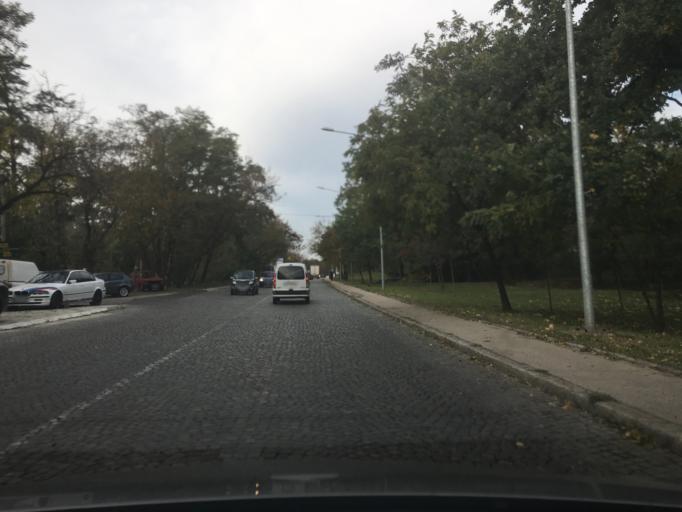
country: RS
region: Central Serbia
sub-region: Belgrade
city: Zemun
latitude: 44.8273
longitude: 20.3918
